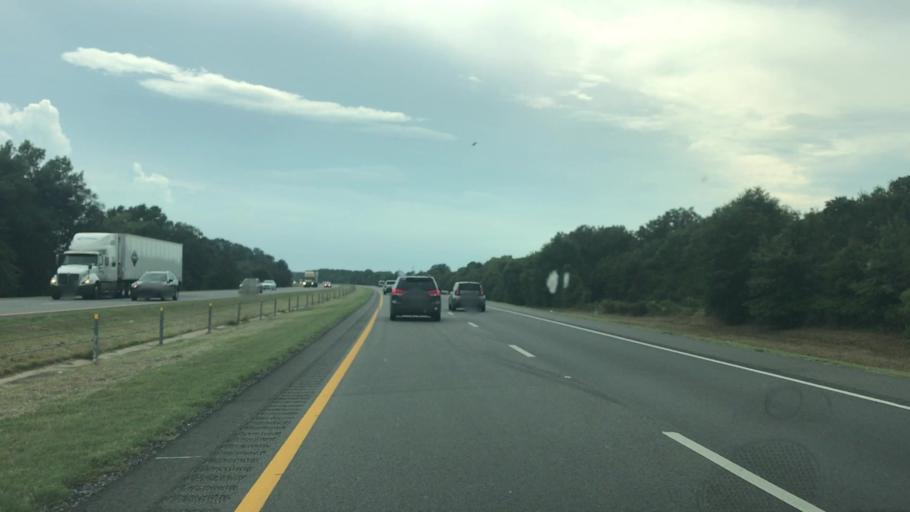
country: US
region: Arkansas
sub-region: Monroe County
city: Brinkley
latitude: 34.9010
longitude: -91.2373
